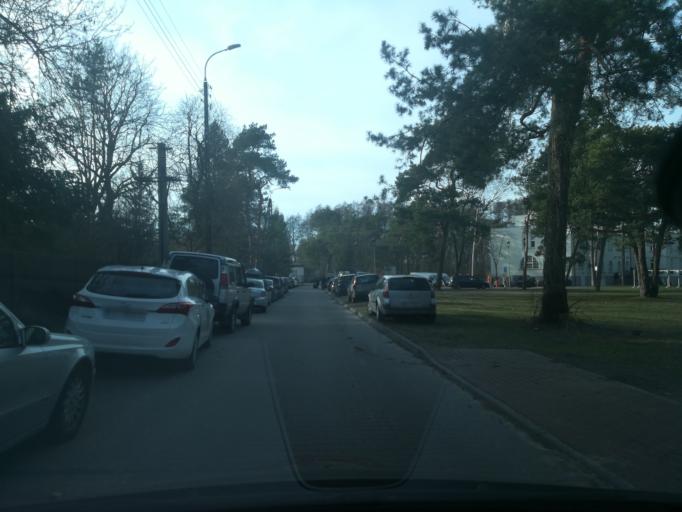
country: PL
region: Masovian Voivodeship
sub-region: Powiat piaseczynski
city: Konstancin-Jeziorna
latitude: 52.0849
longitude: 21.1102
